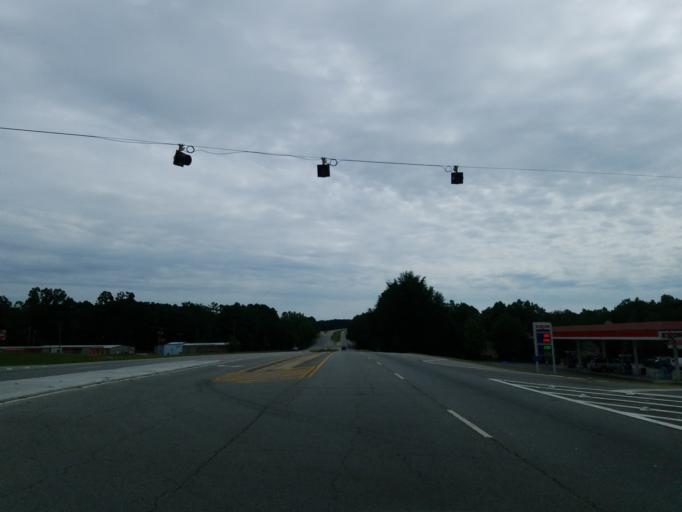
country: US
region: Georgia
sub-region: Lamar County
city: Barnesville
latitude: 33.0640
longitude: -84.1691
